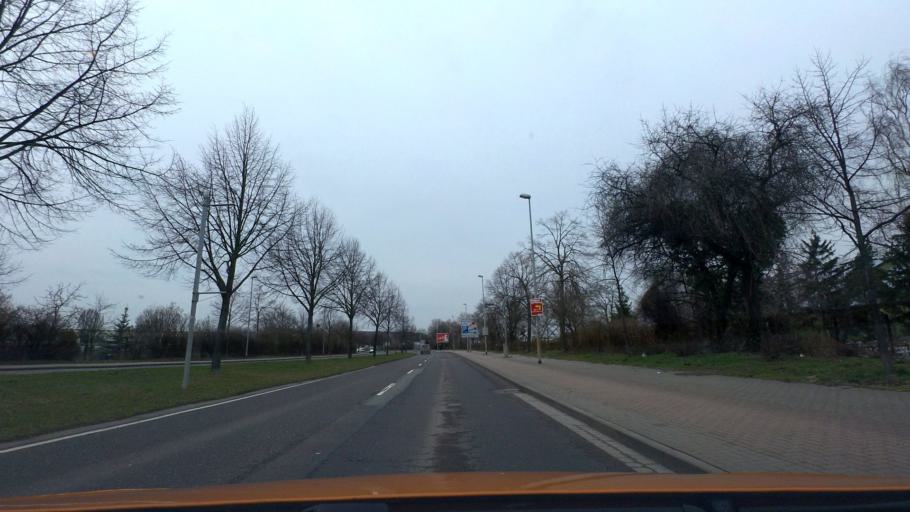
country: DE
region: Saxony-Anhalt
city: Biederitz
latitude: 52.1315
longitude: 11.6768
